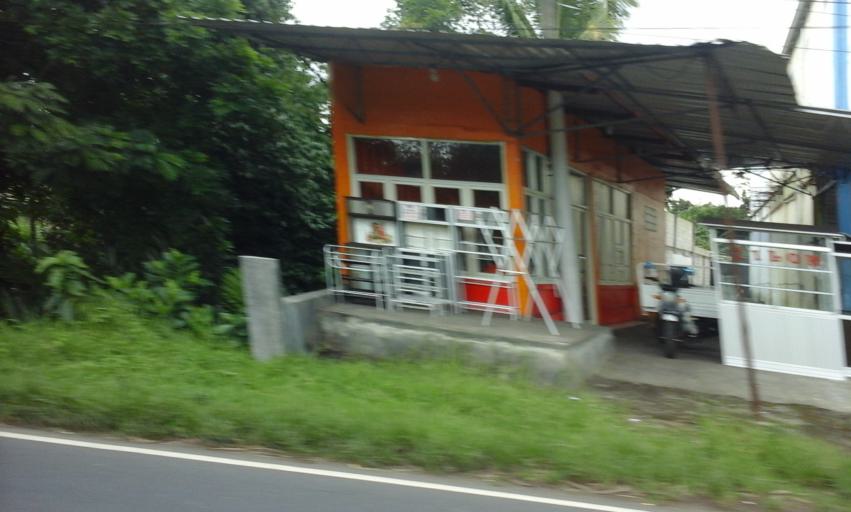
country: ID
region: East Java
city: Jatiroto
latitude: -8.1205
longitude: 113.3553
